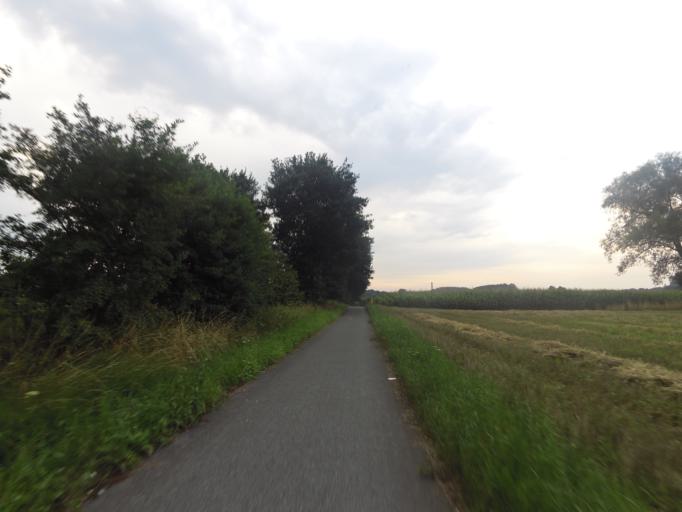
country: NL
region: Gelderland
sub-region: Oude IJsselstreek
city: Gendringen
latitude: 51.8611
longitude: 6.3976
